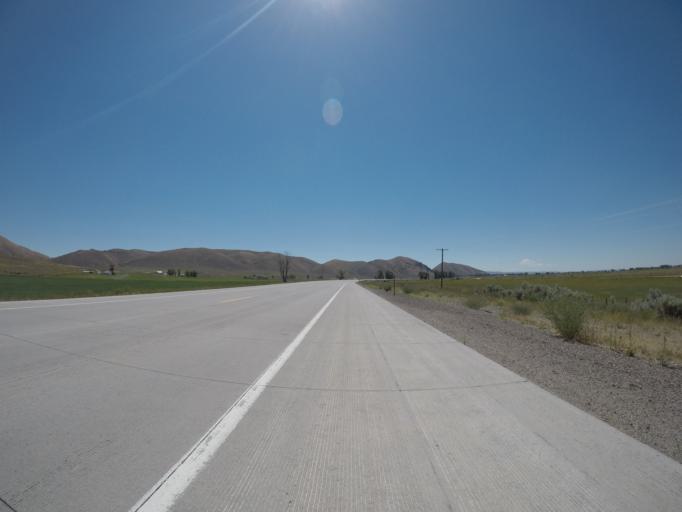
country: US
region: Idaho
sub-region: Bear Lake County
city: Montpelier
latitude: 42.1189
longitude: -110.9622
